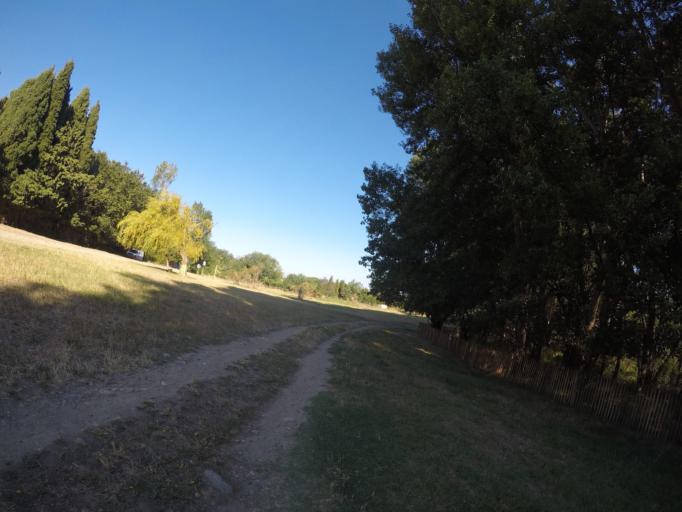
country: FR
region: Languedoc-Roussillon
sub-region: Departement des Pyrenees-Orientales
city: Pezilla-la-Riviere
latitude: 42.6807
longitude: 2.7552
